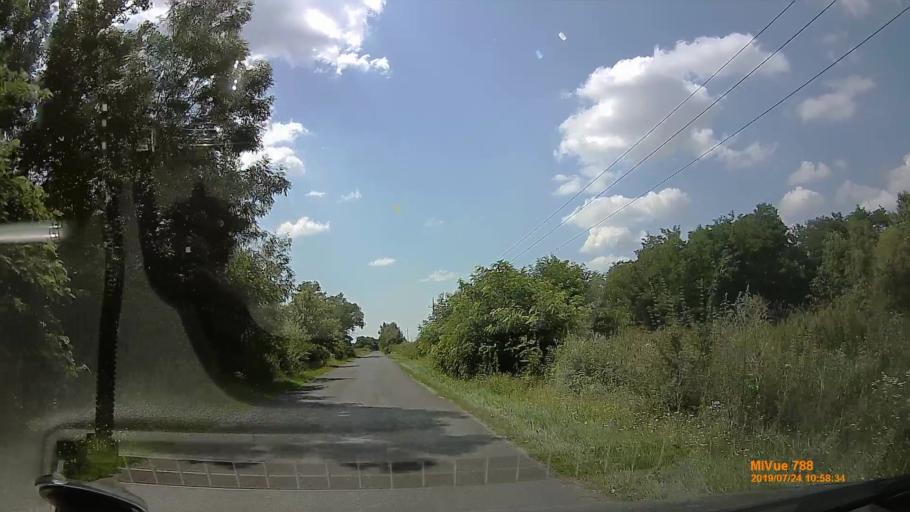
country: HU
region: Szabolcs-Szatmar-Bereg
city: Tarpa
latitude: 48.1759
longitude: 22.5164
